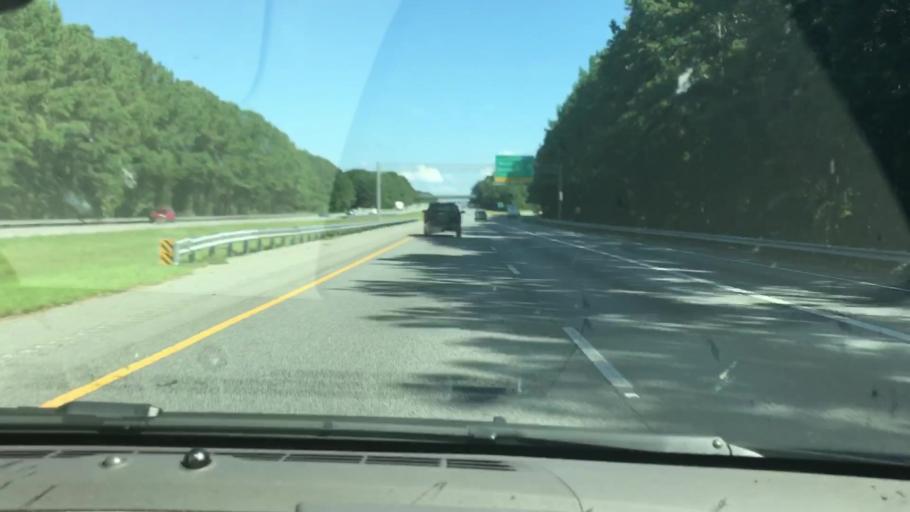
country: US
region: Alabama
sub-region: Russell County
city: Phenix City
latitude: 32.5593
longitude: -84.9624
